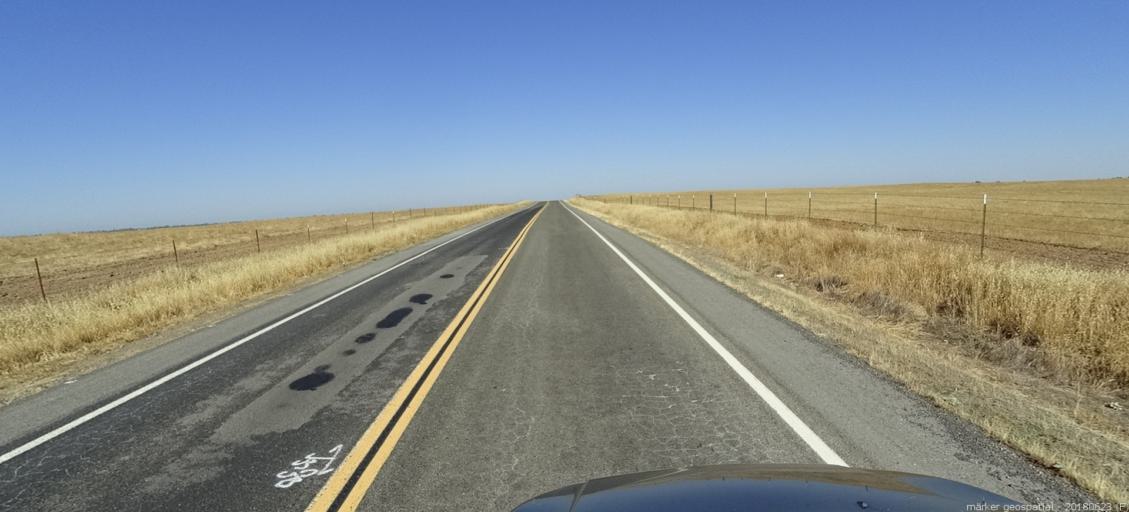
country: US
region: California
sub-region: Madera County
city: Bonadelle Ranchos-Madera Ranchos
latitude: 36.9668
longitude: -119.8311
